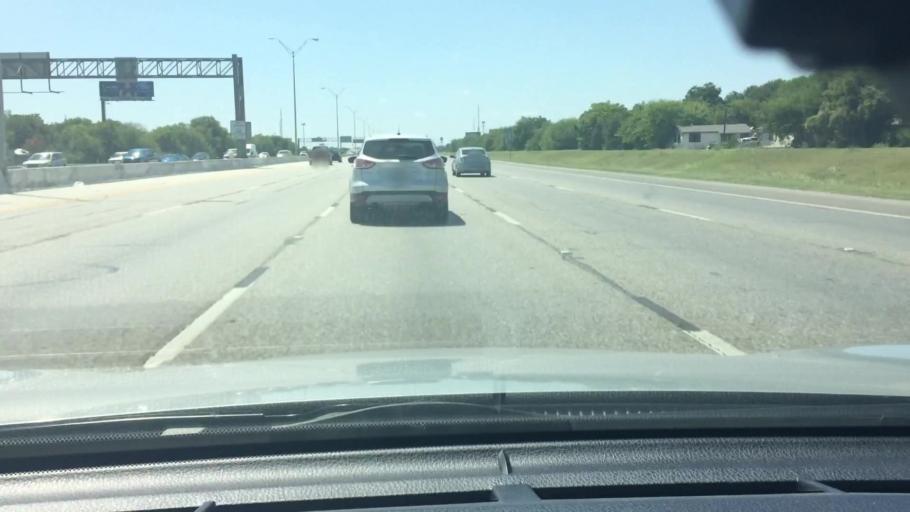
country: US
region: Texas
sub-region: Bexar County
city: Lackland Air Force Base
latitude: 29.4057
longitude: -98.5658
